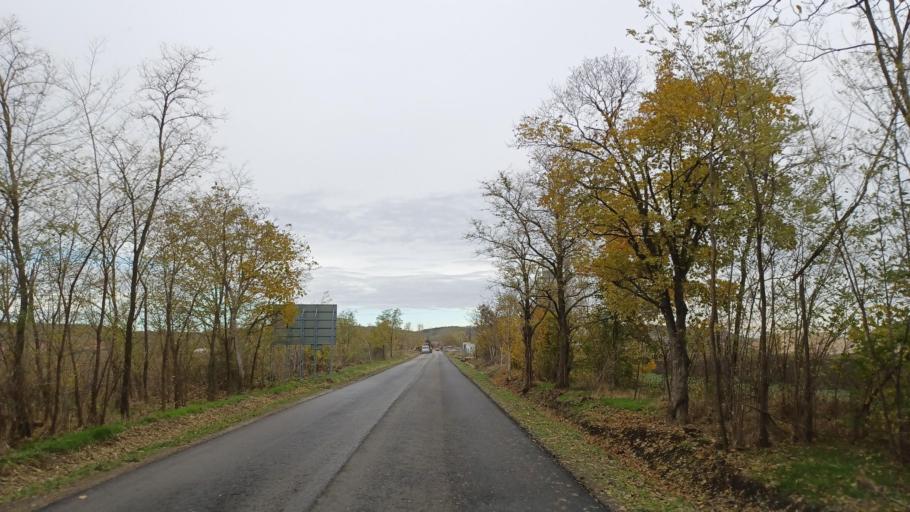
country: HU
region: Tolna
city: Dunaszentgyorgy
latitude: 46.5221
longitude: 18.7738
